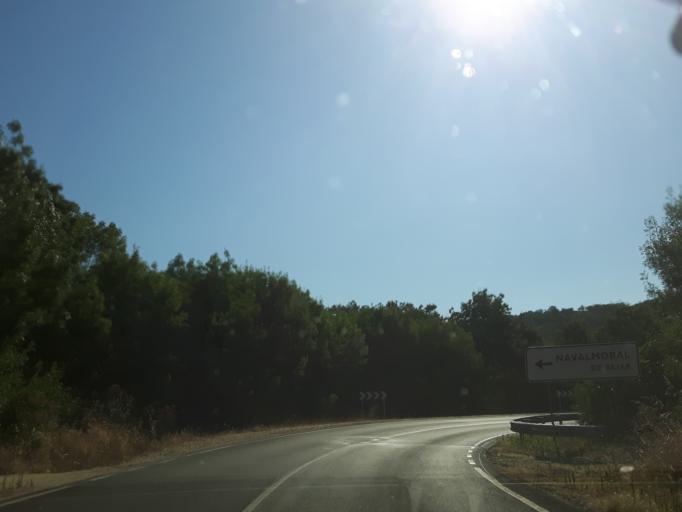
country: ES
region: Castille and Leon
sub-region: Provincia de Salamanca
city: Navalmoral de Bejar
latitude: 40.4153
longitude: -5.8001
